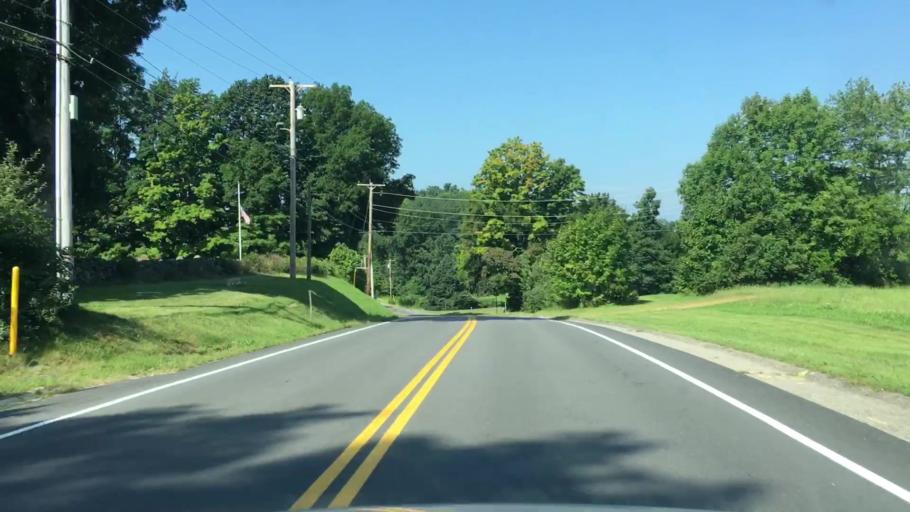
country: US
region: New Hampshire
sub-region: Rockingham County
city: East Kingston
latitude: 42.9228
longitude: -71.0002
